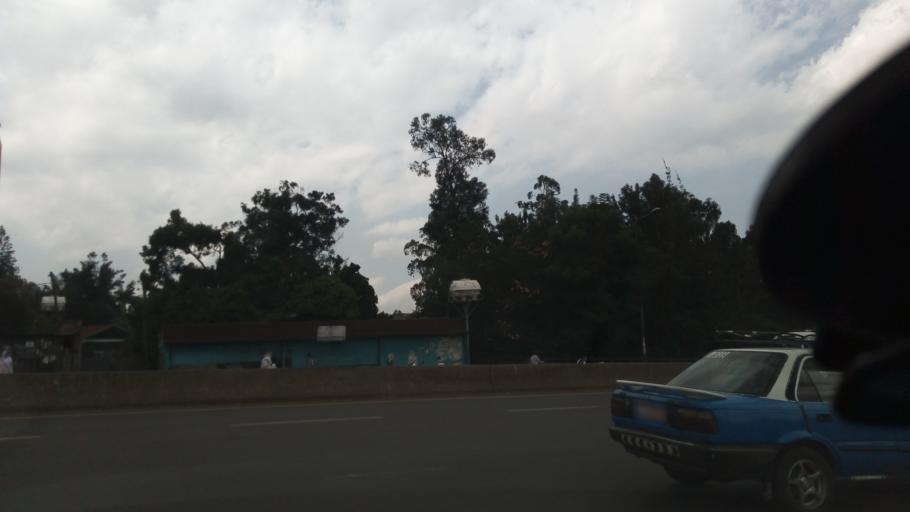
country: ET
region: Adis Abeba
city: Addis Ababa
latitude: 8.9937
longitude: 38.7173
